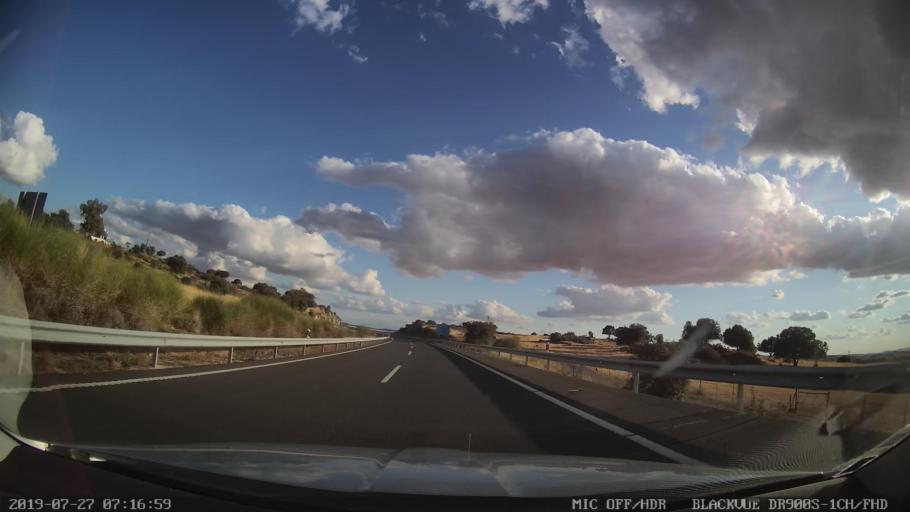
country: ES
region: Extremadura
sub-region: Provincia de Caceres
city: Trujillo
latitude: 39.4478
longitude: -5.8739
